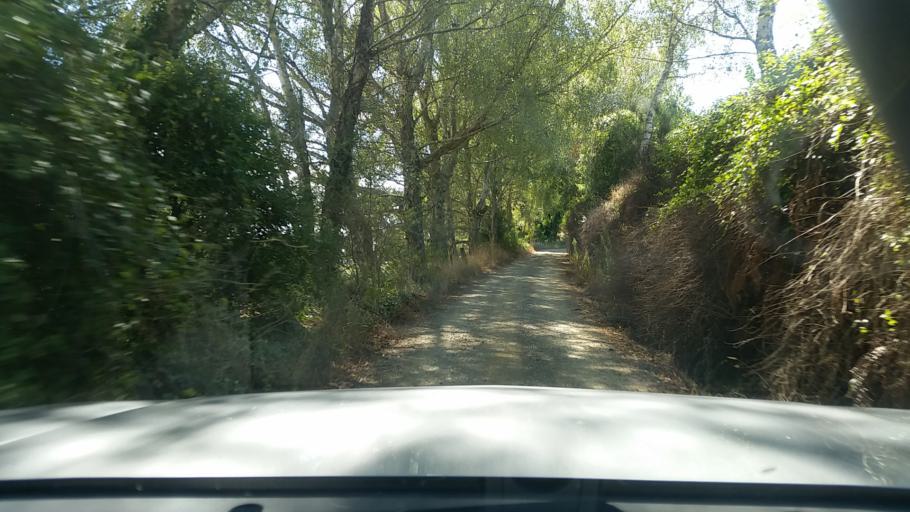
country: NZ
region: Nelson
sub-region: Nelson City
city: Nelson
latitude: -41.2493
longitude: 173.5846
